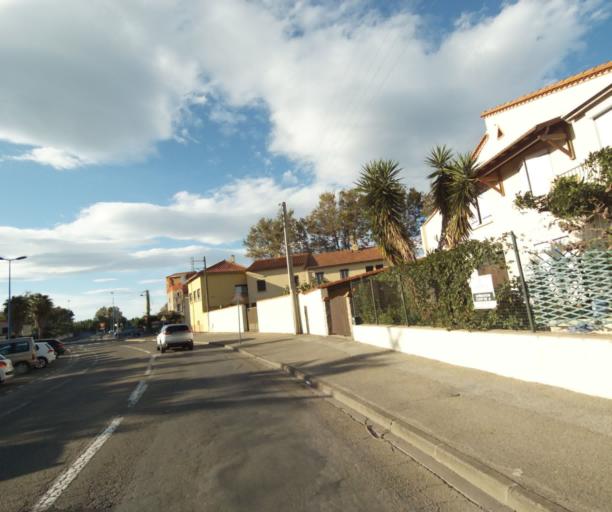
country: FR
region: Languedoc-Roussillon
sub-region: Departement des Pyrenees-Orientales
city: Argelers
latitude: 42.5494
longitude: 3.0324
